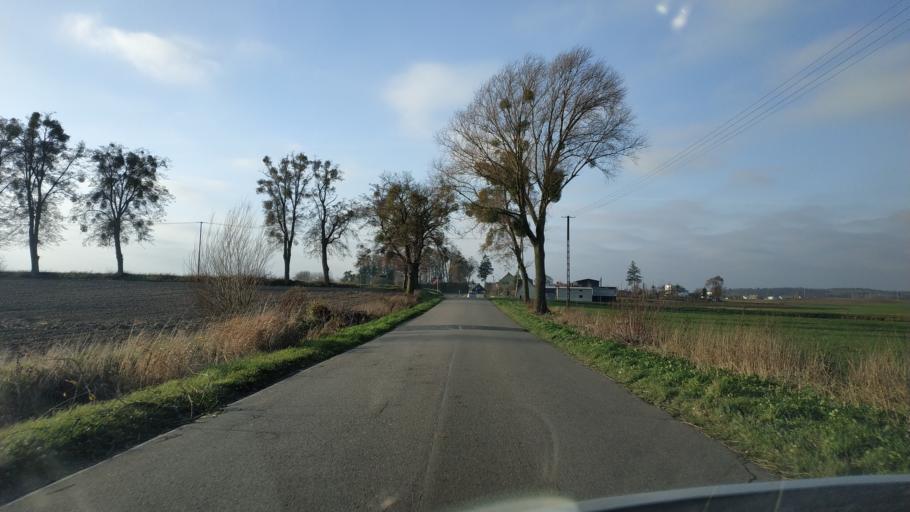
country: PL
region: Warmian-Masurian Voivodeship
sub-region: Powiat nowomiejski
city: Biskupiec
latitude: 53.4465
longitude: 19.3643
